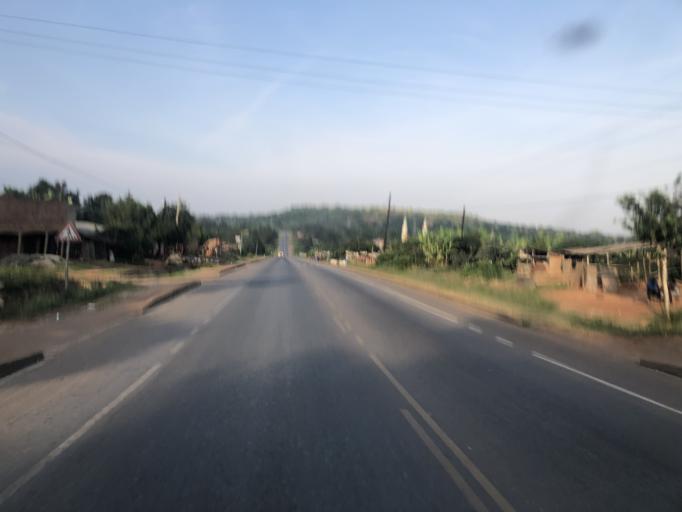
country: UG
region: Central Region
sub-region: Mpigi District
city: Mpigi
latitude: 0.1721
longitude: 32.2640
